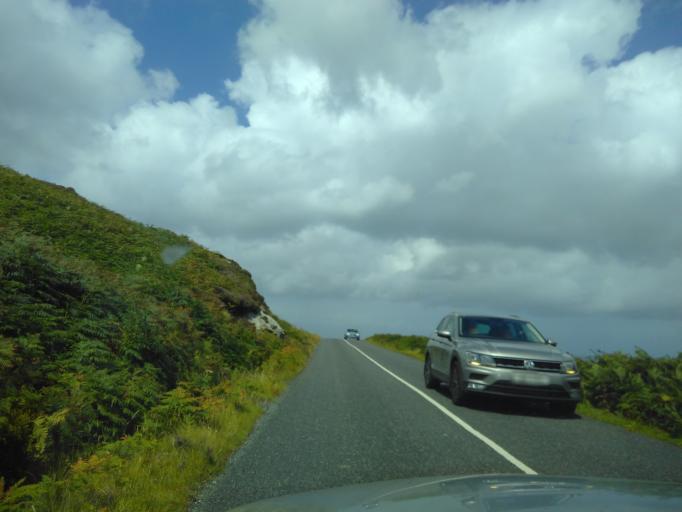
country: IE
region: Ulster
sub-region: County Donegal
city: Buncrana
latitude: 55.1847
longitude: -7.5868
